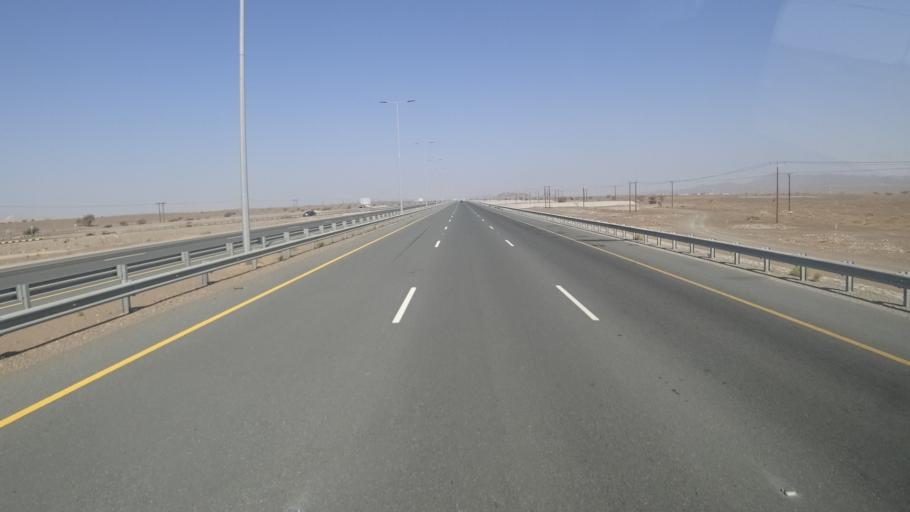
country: OM
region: Ash Sharqiyah
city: Al Qabil
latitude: 22.5343
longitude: 58.7324
